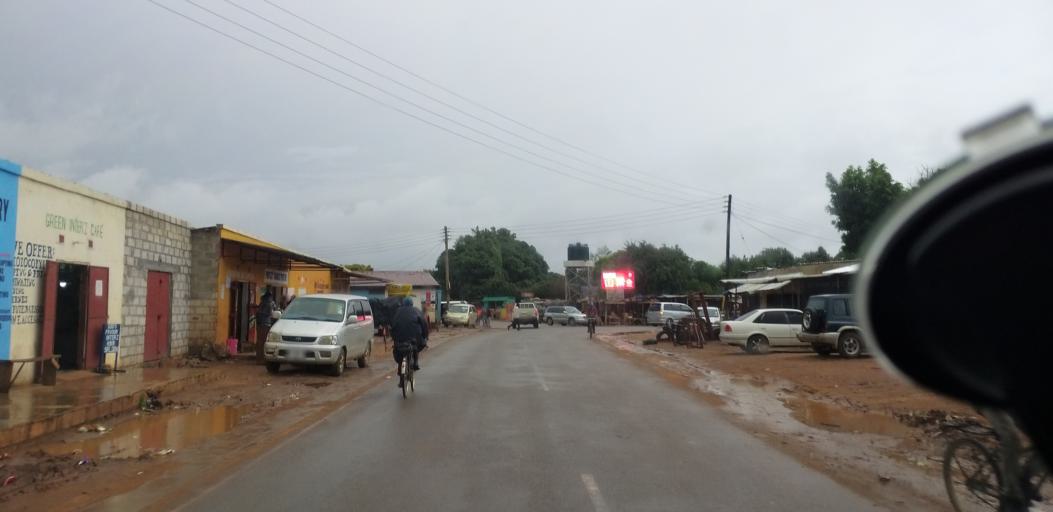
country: ZM
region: Lusaka
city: Lusaka
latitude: -15.5134
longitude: 28.2988
